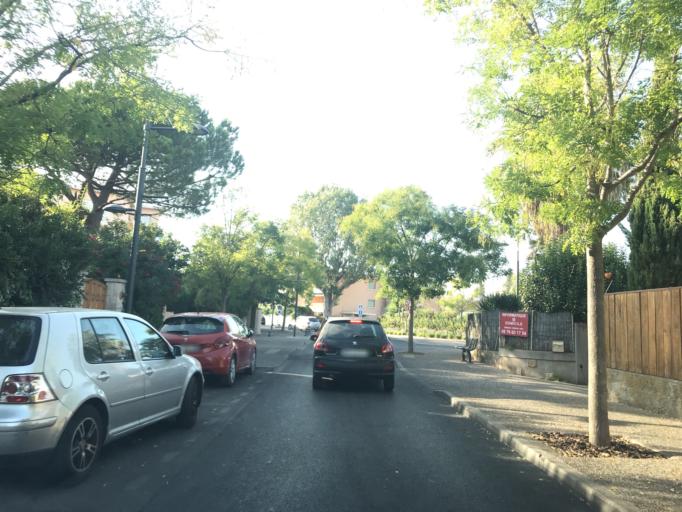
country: FR
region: Provence-Alpes-Cote d'Azur
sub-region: Departement du Var
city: Sanary-sur-Mer
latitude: 43.1160
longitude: 5.8097
